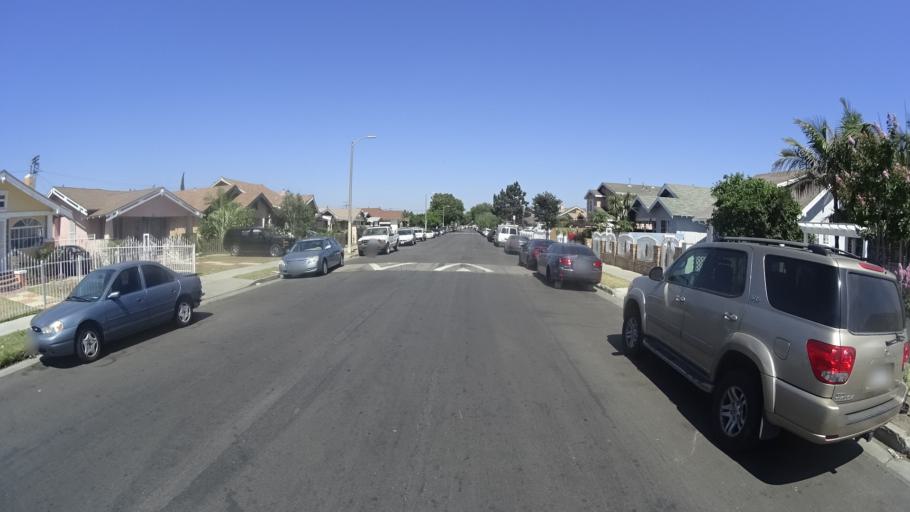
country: US
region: California
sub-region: Los Angeles County
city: Westmont
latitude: 33.9941
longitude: -118.2950
